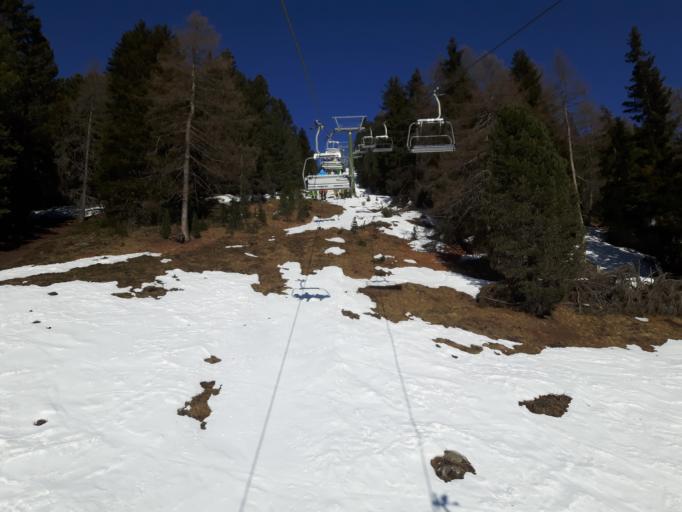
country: IT
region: Trentino-Alto Adige
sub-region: Provincia di Trento
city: Panchia
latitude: 46.3435
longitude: 11.5416
